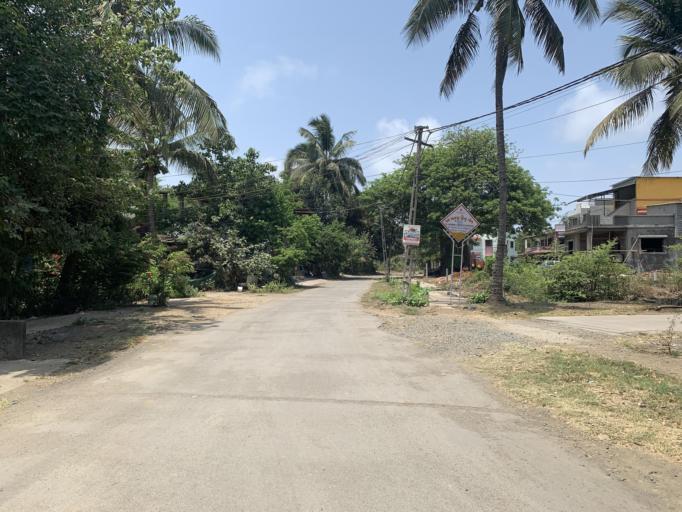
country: IN
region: Daman and Diu
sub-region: Daman District
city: Daman
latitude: 20.4553
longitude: 72.8486
